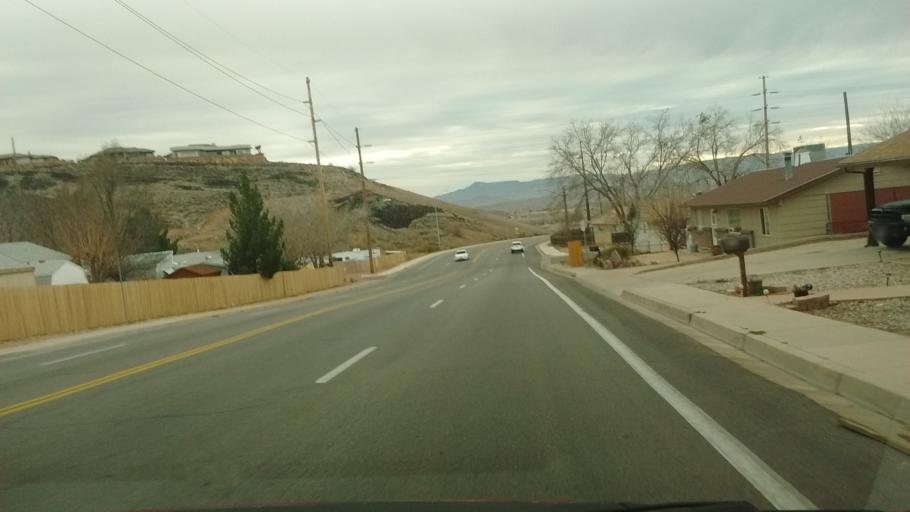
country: US
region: Utah
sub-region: Washington County
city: Washington
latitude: 37.1285
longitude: -113.5050
